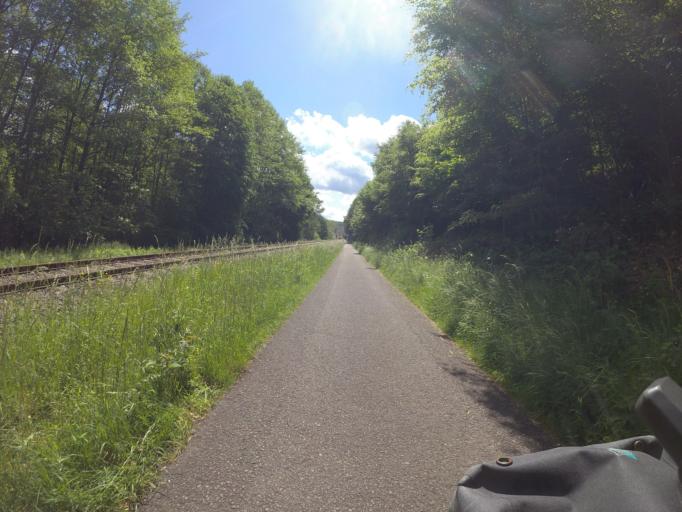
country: DE
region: Rheinland-Pfalz
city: Dahn
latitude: 49.1636
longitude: 7.7593
